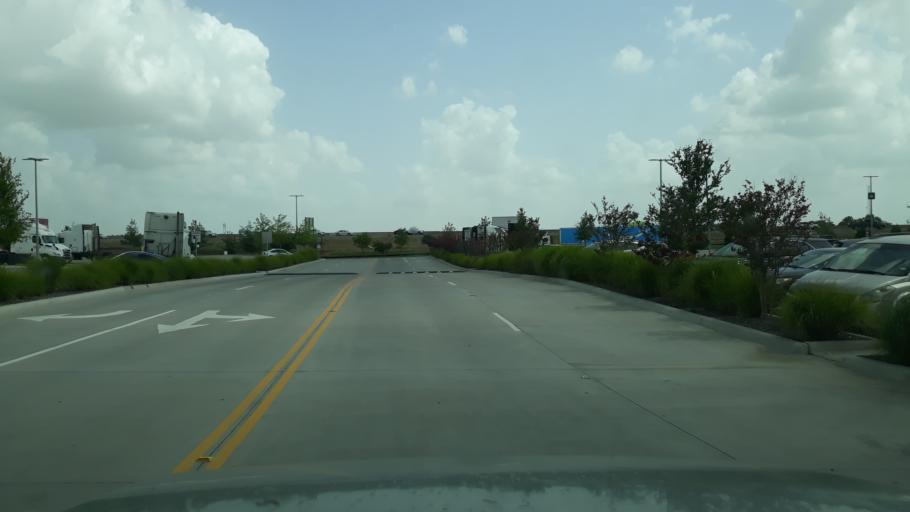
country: US
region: Texas
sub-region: Dallas County
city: Coppell
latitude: 32.9500
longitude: -97.0300
